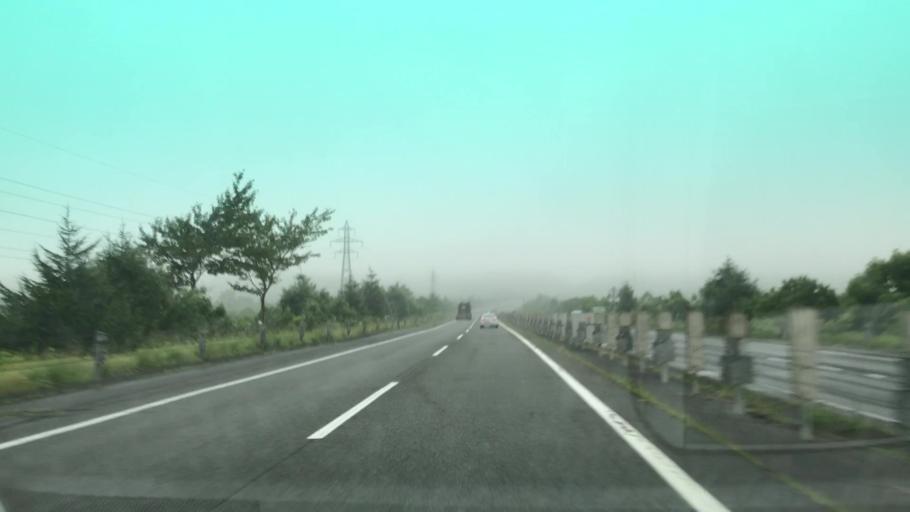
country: JP
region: Hokkaido
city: Tomakomai
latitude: 42.6600
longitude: 141.5787
